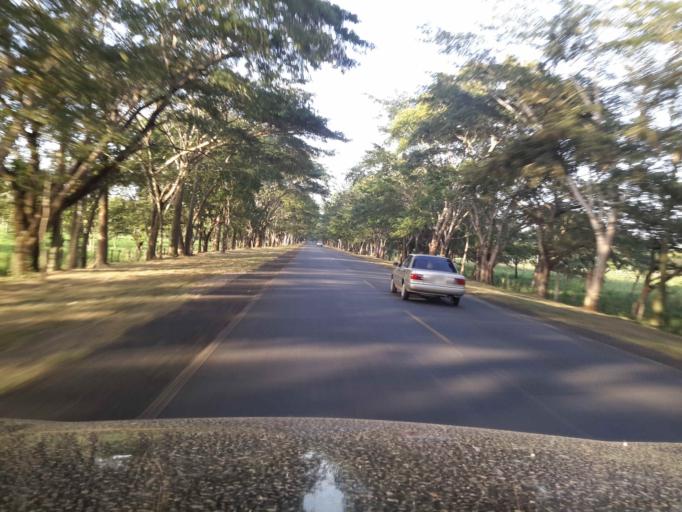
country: NI
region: Rio San Juan
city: San Miguelito
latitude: 11.4498
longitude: -84.8509
